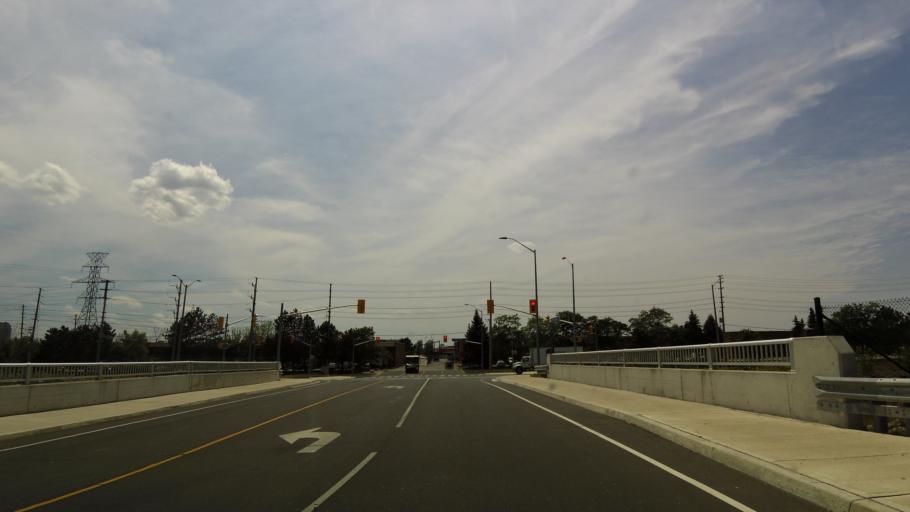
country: CA
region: Ontario
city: Etobicoke
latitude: 43.6378
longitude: -79.6083
